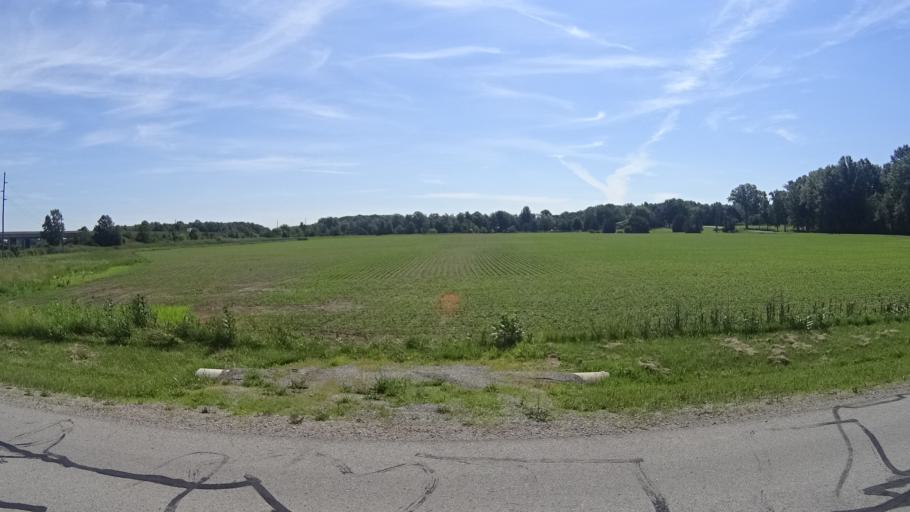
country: US
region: Ohio
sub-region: Erie County
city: Huron
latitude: 41.3660
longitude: -82.4580
